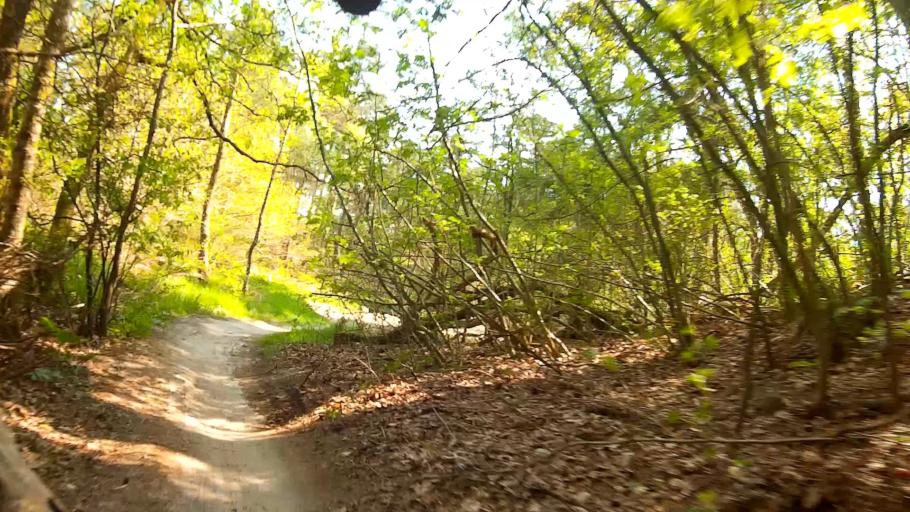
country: NL
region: Utrecht
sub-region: Gemeente Baarn
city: Baarn
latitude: 52.1902
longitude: 5.2519
